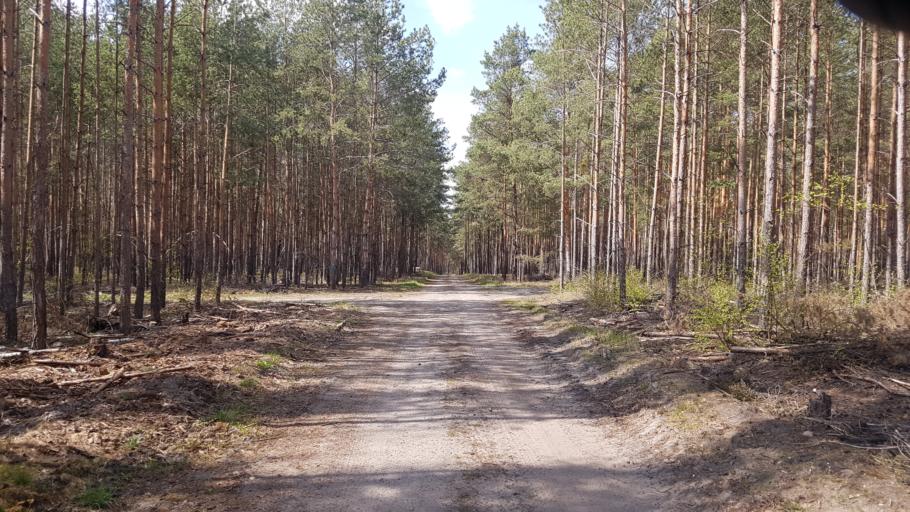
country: DE
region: Brandenburg
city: Ruckersdorf
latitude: 51.5514
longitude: 13.6364
